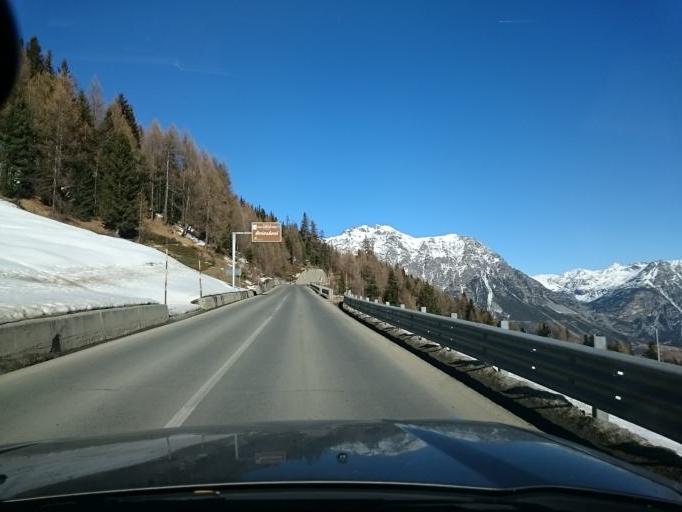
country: IT
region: Lombardy
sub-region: Provincia di Sondrio
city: Isolaccia
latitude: 46.4692
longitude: 10.2496
